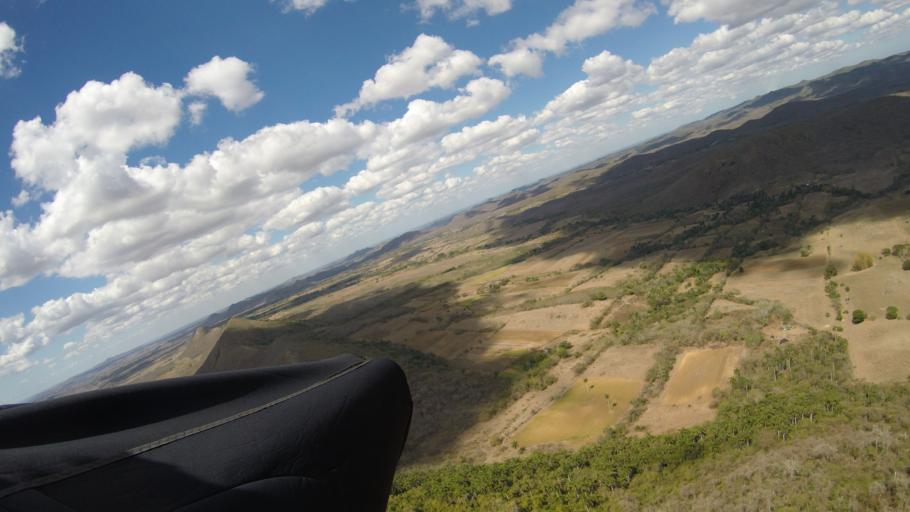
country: CU
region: Villa Clara
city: Manicaragua
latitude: 22.2116
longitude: -79.8780
